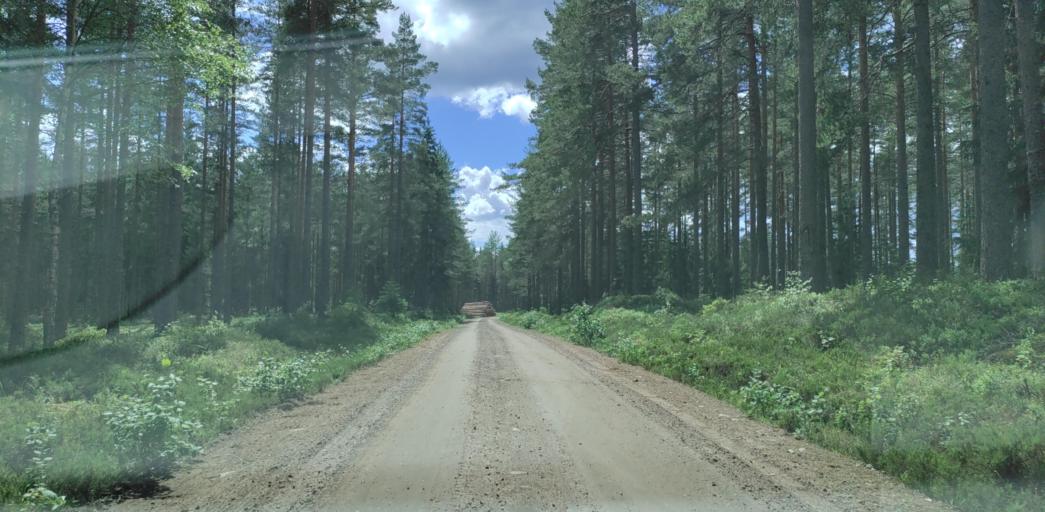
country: SE
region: Vaermland
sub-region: Hagfors Kommun
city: Ekshaerad
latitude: 60.0696
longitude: 13.3094
